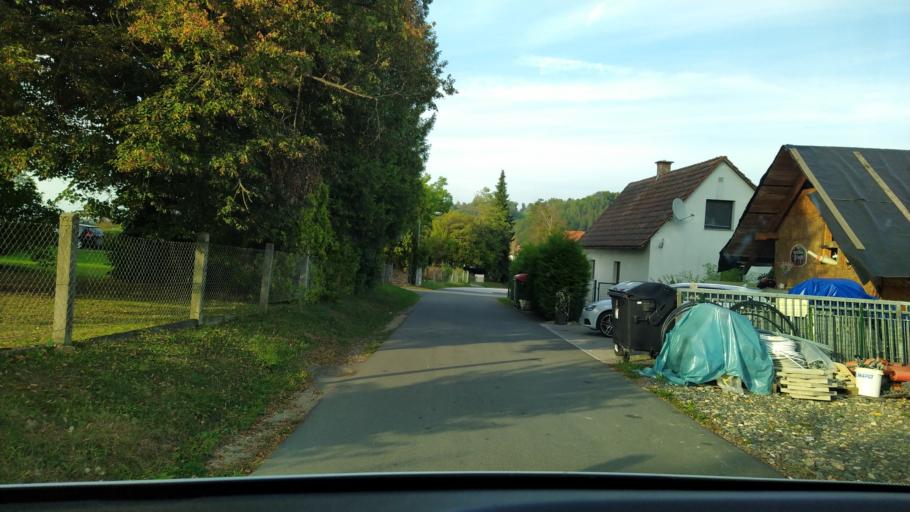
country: AT
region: Styria
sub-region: Politischer Bezirk Leibnitz
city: Arnfels
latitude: 46.6748
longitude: 15.3927
